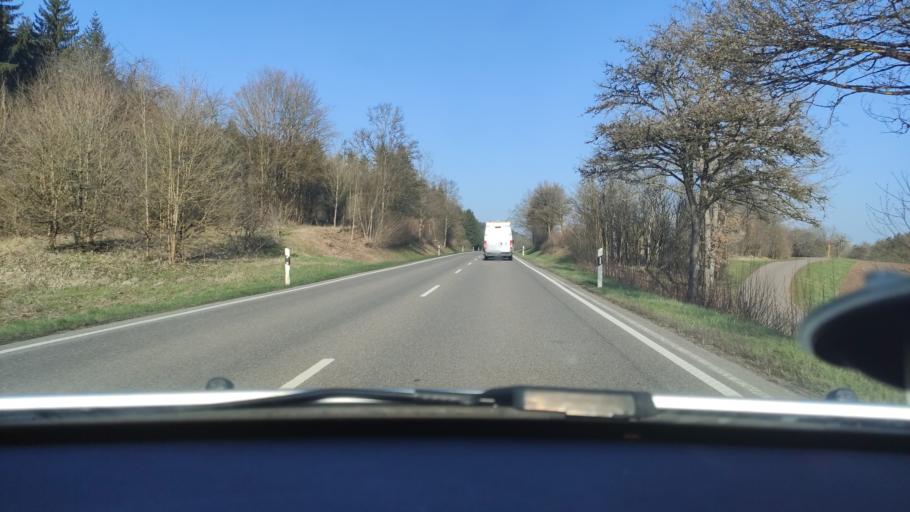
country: DE
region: Baden-Wuerttemberg
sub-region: Tuebingen Region
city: Grosselfingen
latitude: 48.3236
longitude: 8.8561
